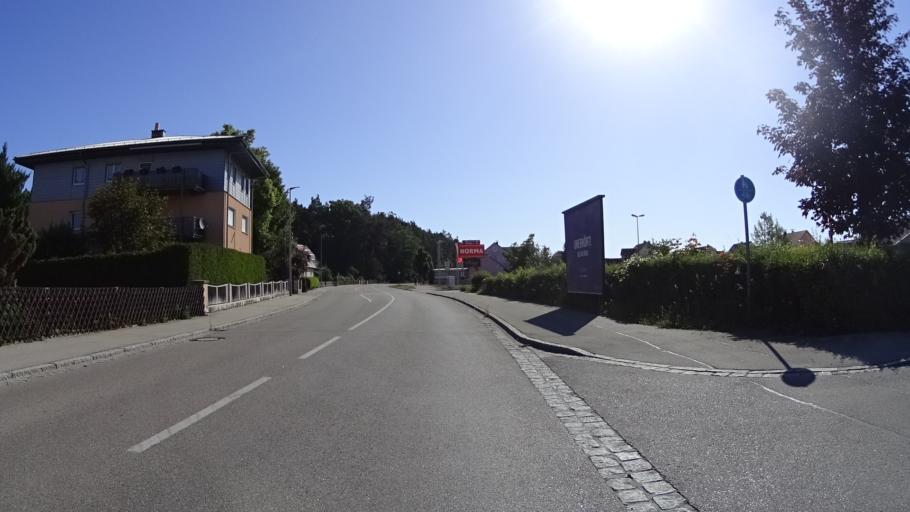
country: DE
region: Bavaria
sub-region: Regierungsbezirk Mittelfranken
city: Arberg
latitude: 49.1584
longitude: 10.5591
